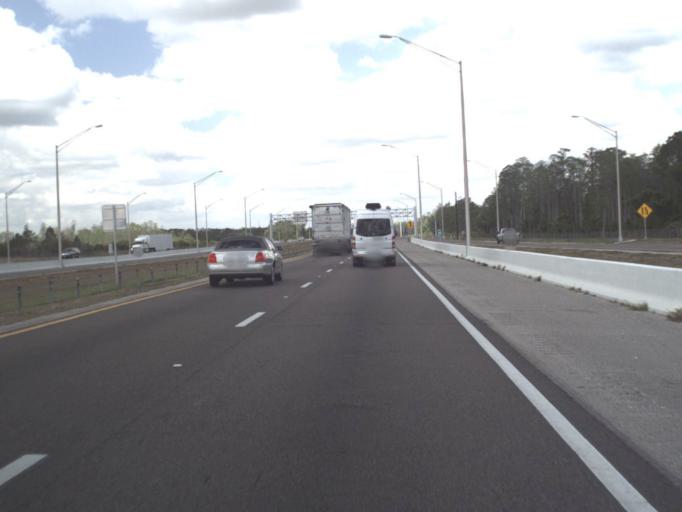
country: US
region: Florida
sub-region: Orange County
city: Wedgefield
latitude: 28.4522
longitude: -81.0590
